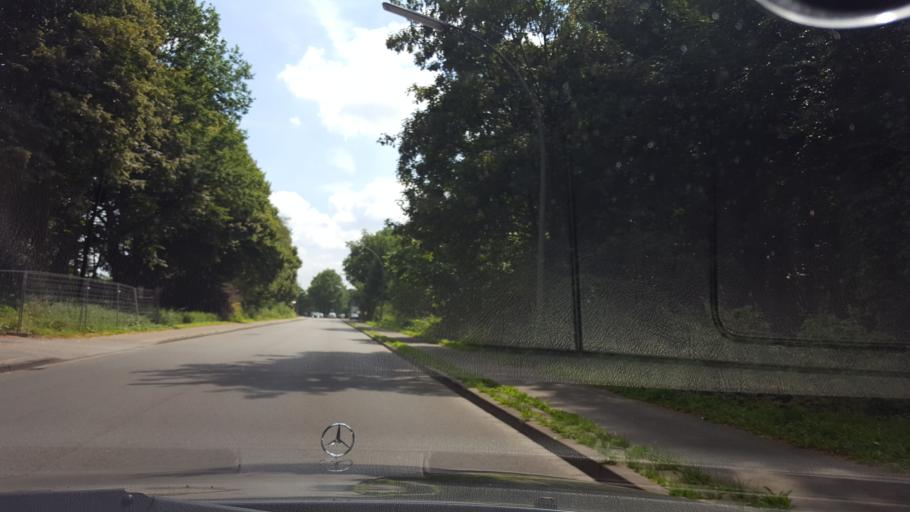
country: DE
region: North Rhine-Westphalia
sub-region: Regierungsbezirk Munster
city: Recklinghausen
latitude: 51.6646
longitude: 7.1733
